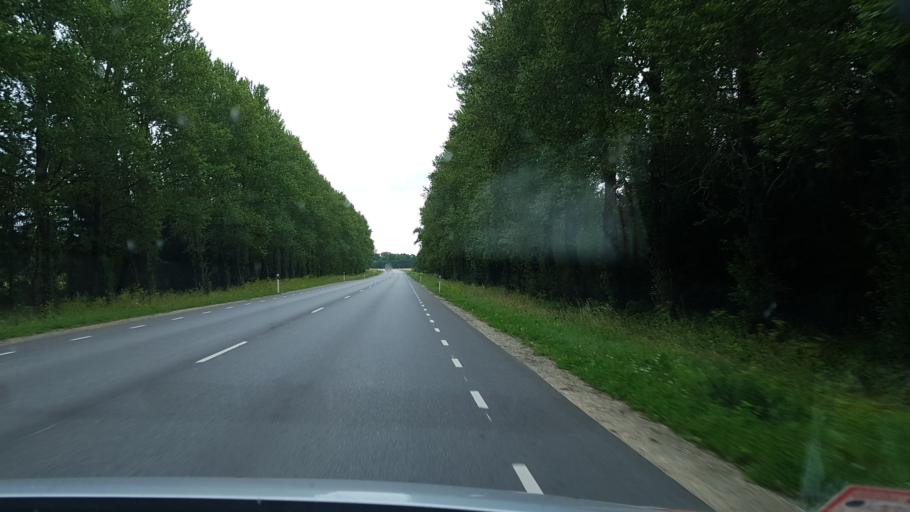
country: EE
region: Polvamaa
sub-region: Polva linn
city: Polva
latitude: 58.2768
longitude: 27.0024
